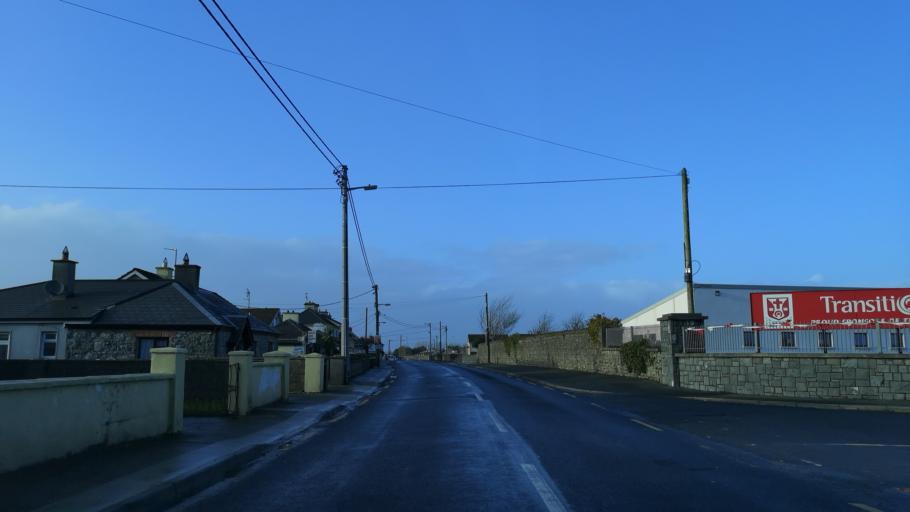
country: IE
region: Connaught
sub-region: County Galway
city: Tuam
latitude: 53.5069
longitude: -8.8380
